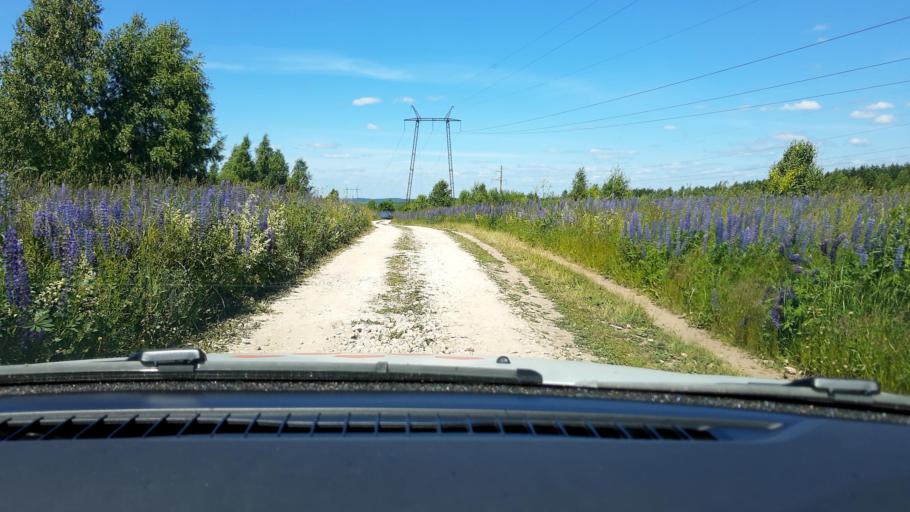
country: RU
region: Nizjnij Novgorod
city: Surovatikha
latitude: 55.8708
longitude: 43.9744
